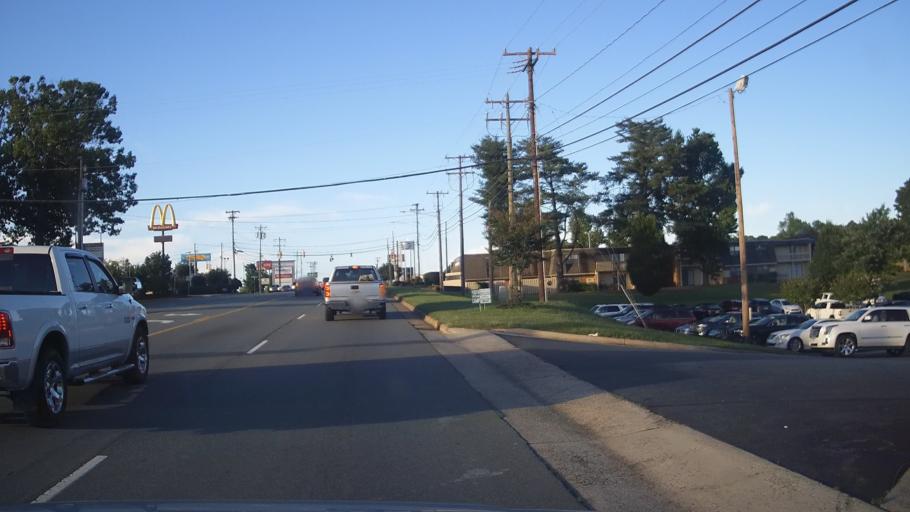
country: US
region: North Carolina
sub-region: Alamance County
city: Elon
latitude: 36.0713
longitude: -79.4937
